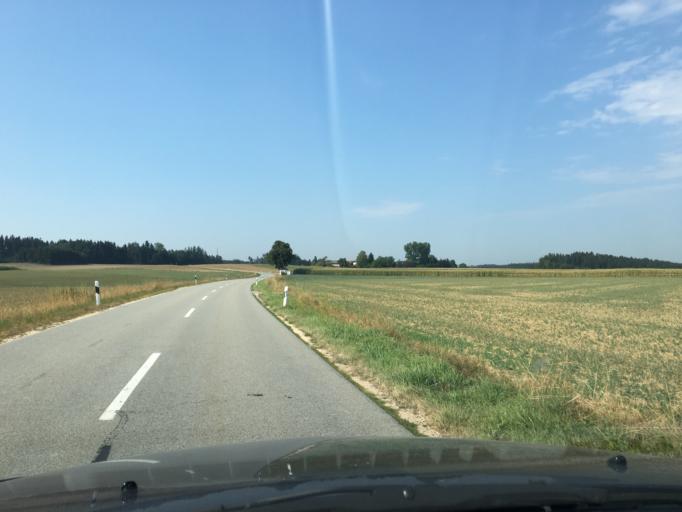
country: DE
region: Bavaria
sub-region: Upper Bavaria
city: Niederbergkirchen
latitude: 48.3277
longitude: 12.4815
